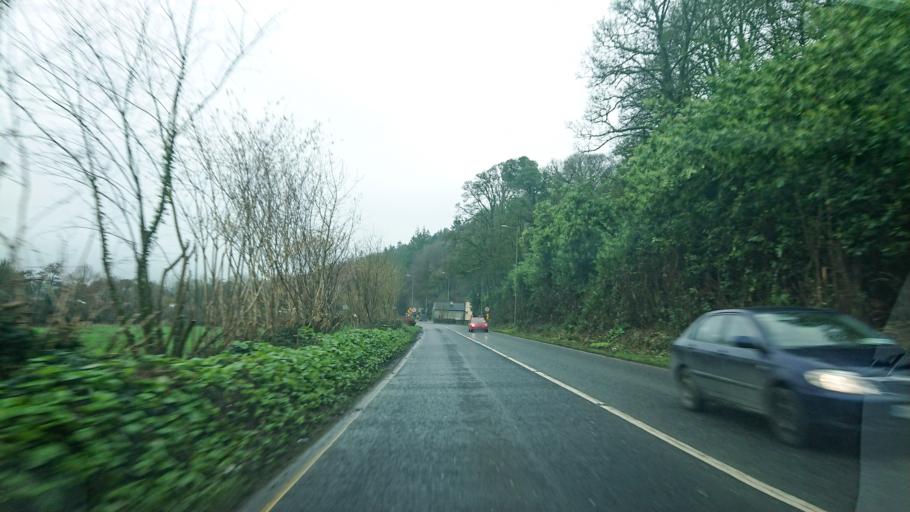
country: IE
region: Munster
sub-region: County Cork
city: Bandon
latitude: 51.7651
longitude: -8.6684
